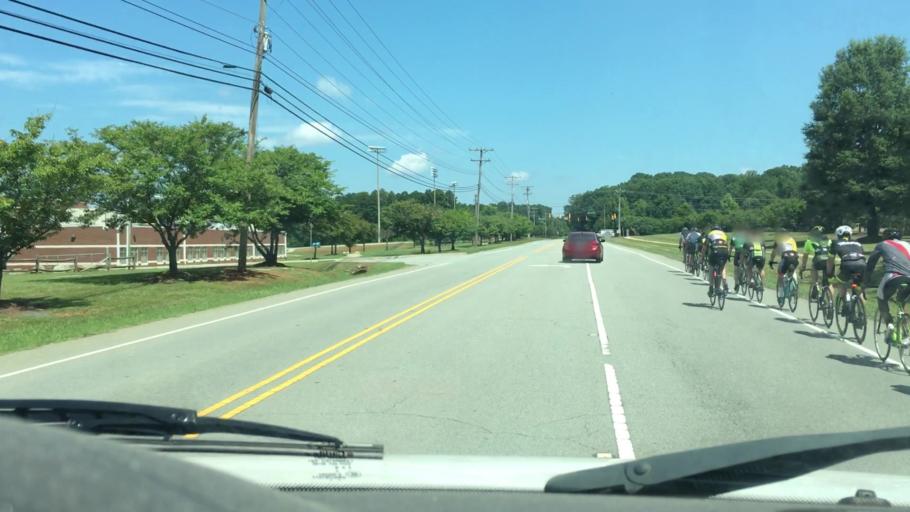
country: US
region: North Carolina
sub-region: Mecklenburg County
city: Huntersville
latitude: 35.3990
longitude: -80.9234
